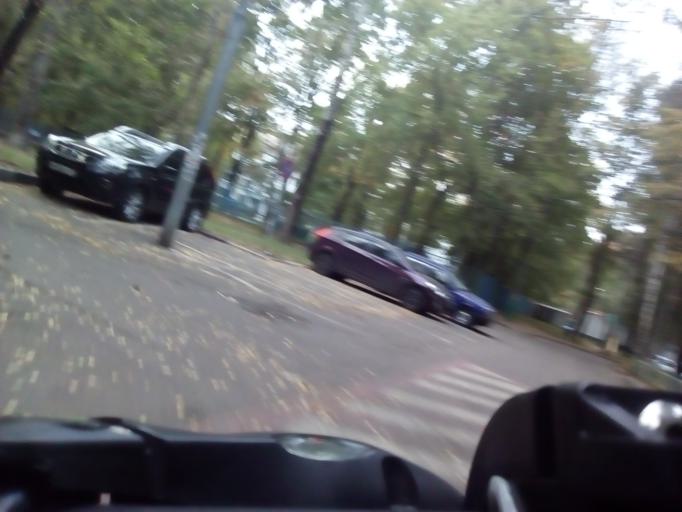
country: RU
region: Moscow
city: Leonovo
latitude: 55.8494
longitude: 37.6418
